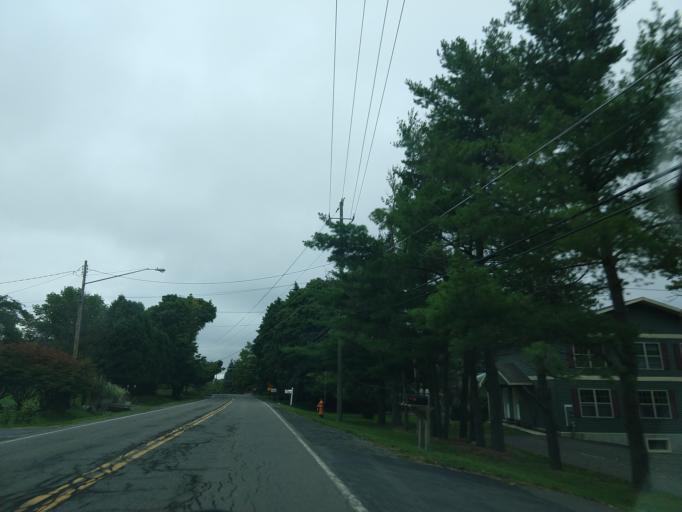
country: US
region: New York
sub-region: Tompkins County
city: South Hill
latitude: 42.4213
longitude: -76.4839
